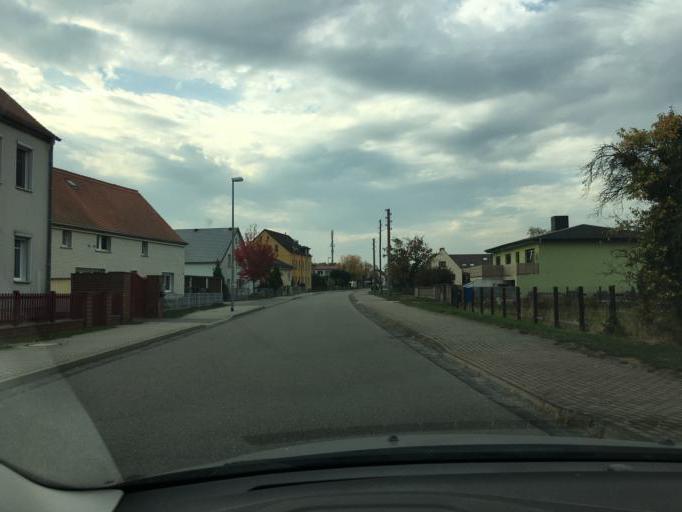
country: DE
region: Saxony
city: Zwochau
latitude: 51.4226
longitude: 12.2970
